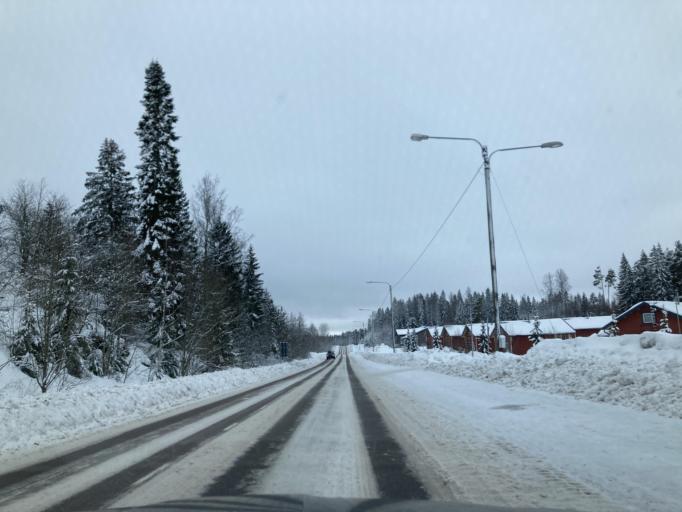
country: FI
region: Central Finland
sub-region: Jaemsae
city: Jaemsae
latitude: 61.8815
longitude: 25.2865
